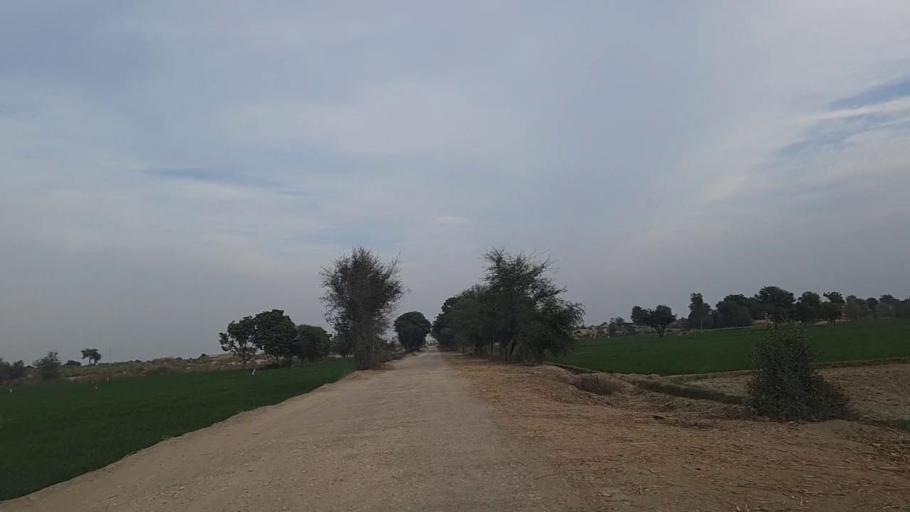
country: PK
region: Sindh
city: Daur
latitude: 26.5103
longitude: 68.4581
